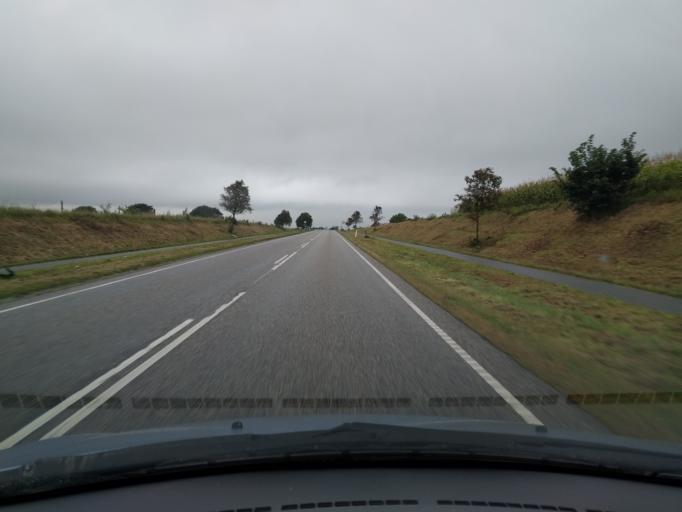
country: DK
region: Zealand
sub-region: Naestved Kommune
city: Naestved
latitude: 55.1854
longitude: 11.7779
